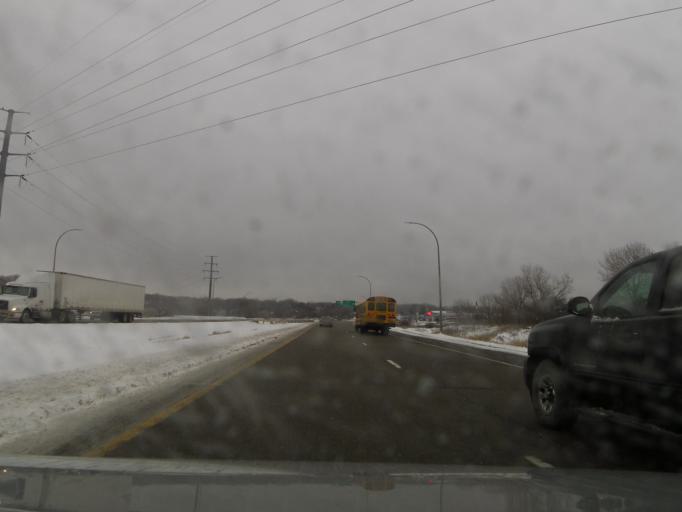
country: US
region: Minnesota
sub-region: Dakota County
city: West Saint Paul
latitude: 44.8768
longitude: -93.0786
